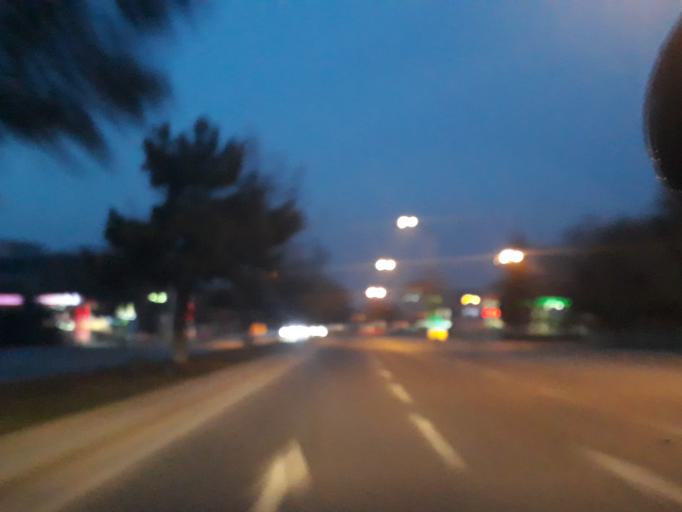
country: TR
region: Konya
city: Selcuklu
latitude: 37.8994
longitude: 32.5083
